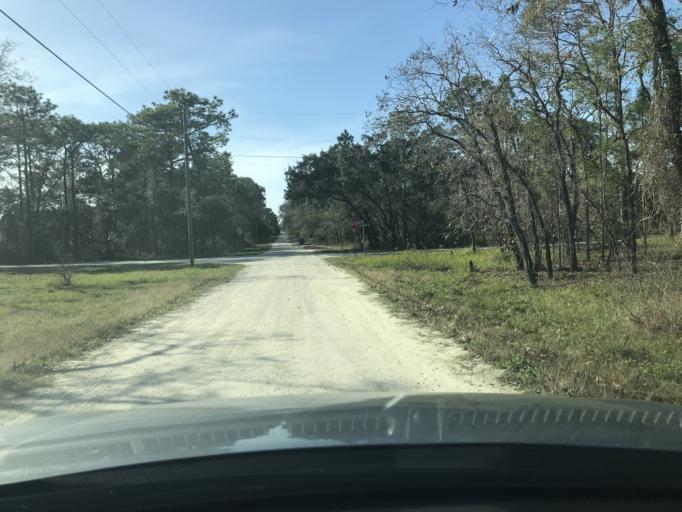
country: US
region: Florida
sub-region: Hernando County
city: North Weeki Wachee
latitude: 28.5517
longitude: -82.5697
